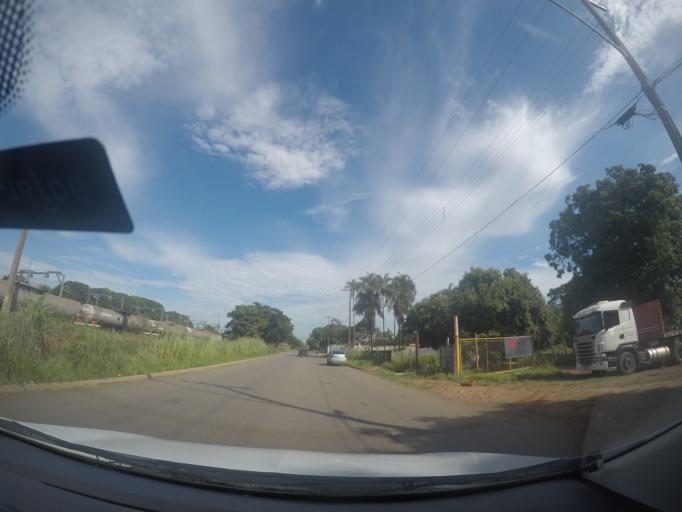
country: BR
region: Goias
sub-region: Goiania
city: Goiania
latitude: -16.6672
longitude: -49.2032
